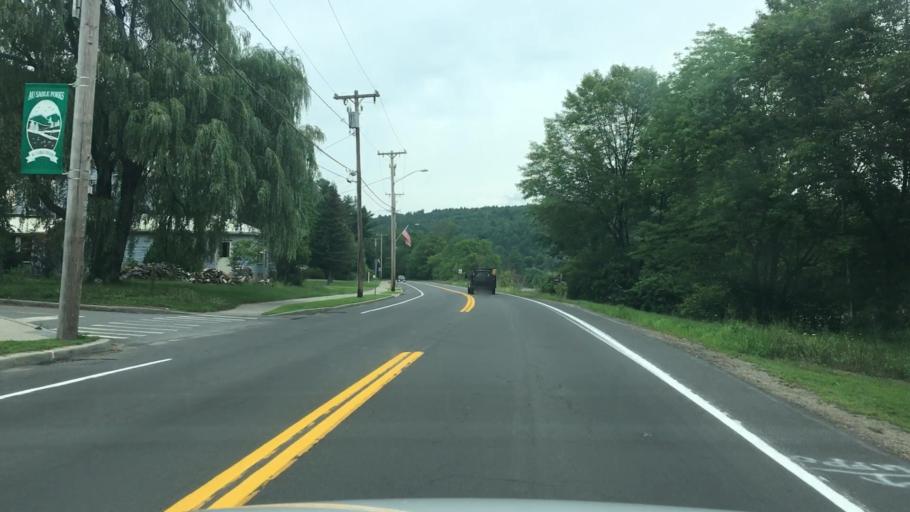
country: US
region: New York
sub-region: Clinton County
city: Peru
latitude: 44.4427
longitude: -73.6669
